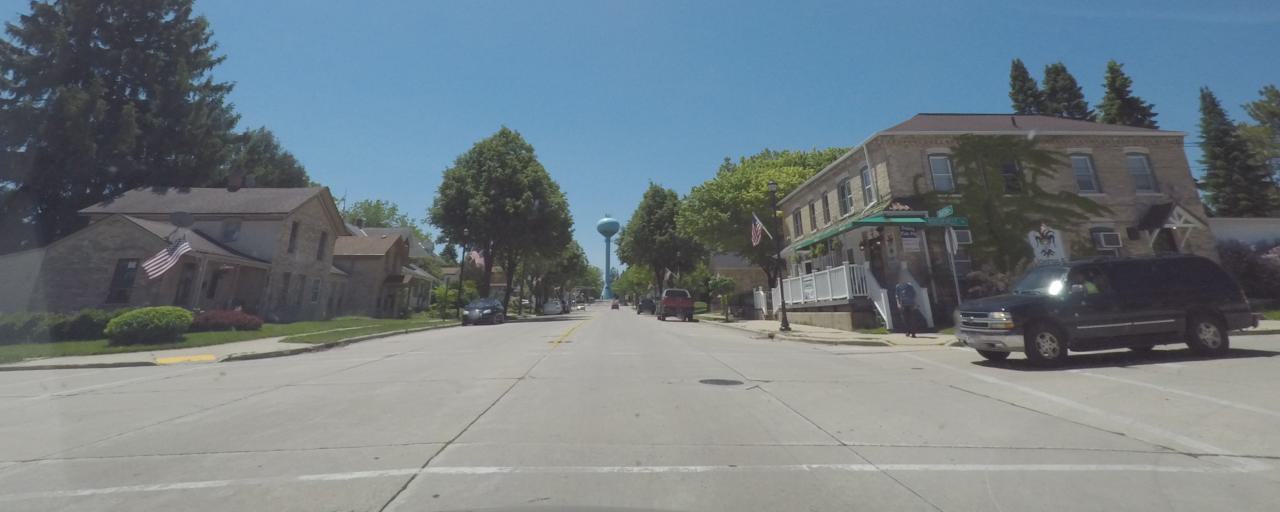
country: US
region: Wisconsin
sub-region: Washington County
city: West Bend
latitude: 43.4406
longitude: -88.1823
